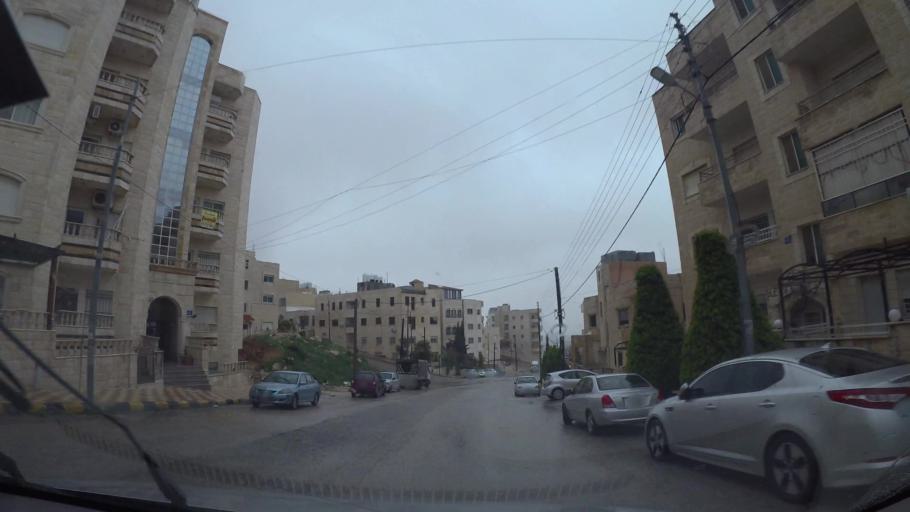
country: JO
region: Amman
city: Al Jubayhah
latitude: 32.0475
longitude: 35.8778
